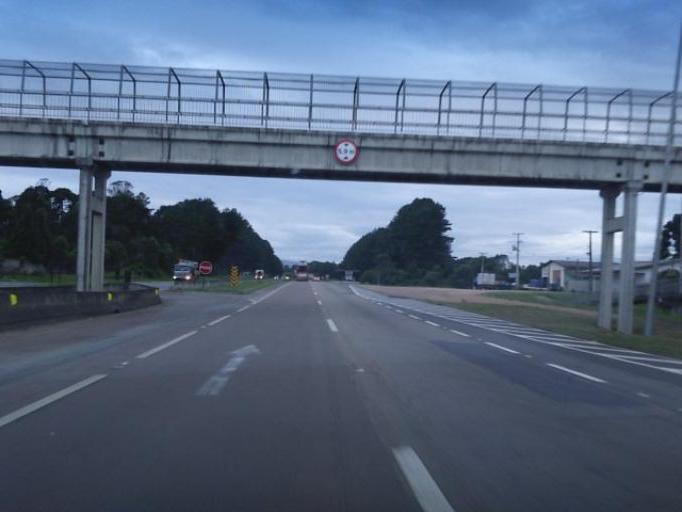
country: BR
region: Parana
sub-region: Sao Jose Dos Pinhais
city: Sao Jose dos Pinhais
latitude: -25.8254
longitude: -49.1228
